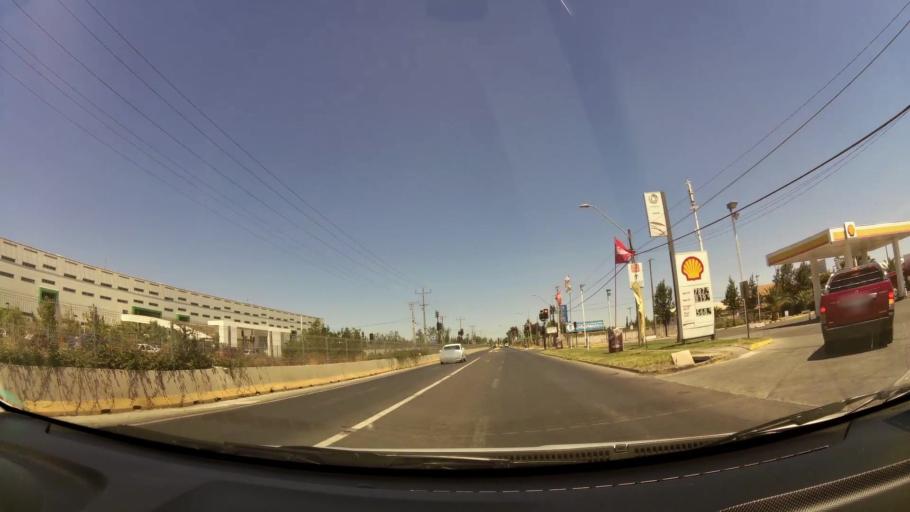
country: CL
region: O'Higgins
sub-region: Provincia de Cachapoal
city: Rancagua
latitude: -34.1539
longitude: -70.7677
